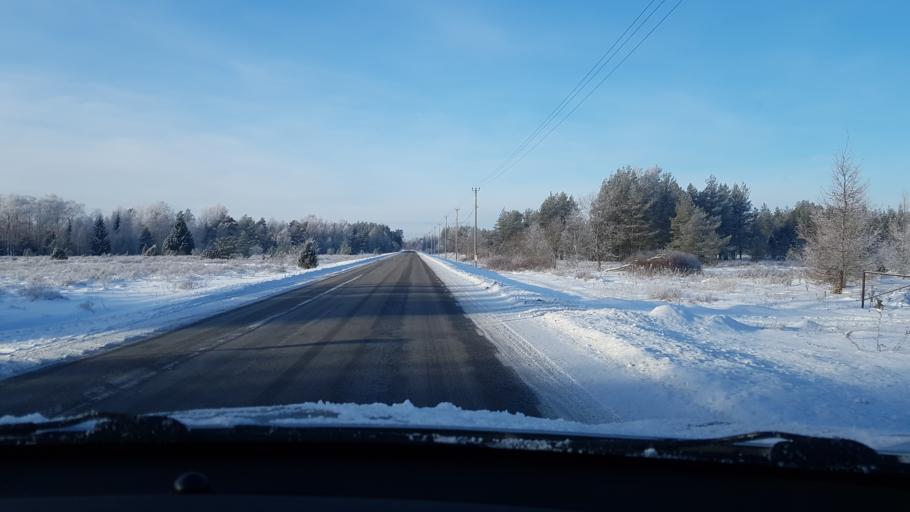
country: EE
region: Harju
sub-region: Keila linn
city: Keila
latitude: 59.3830
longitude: 24.4374
